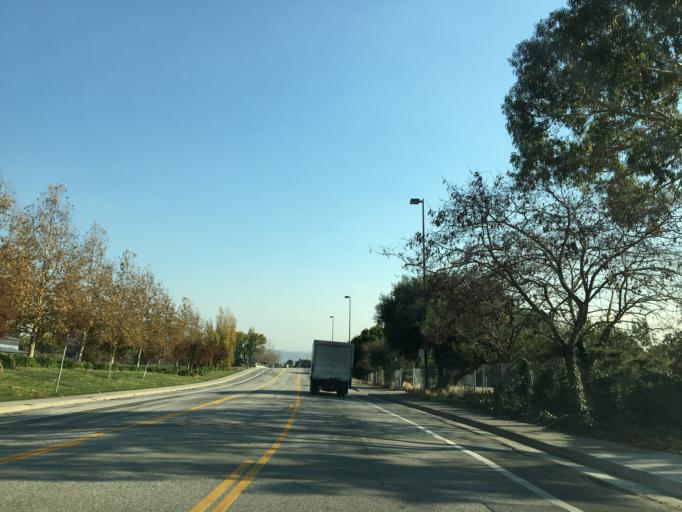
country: US
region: California
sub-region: Santa Clara County
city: Santa Clara
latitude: 37.4105
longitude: -121.9811
